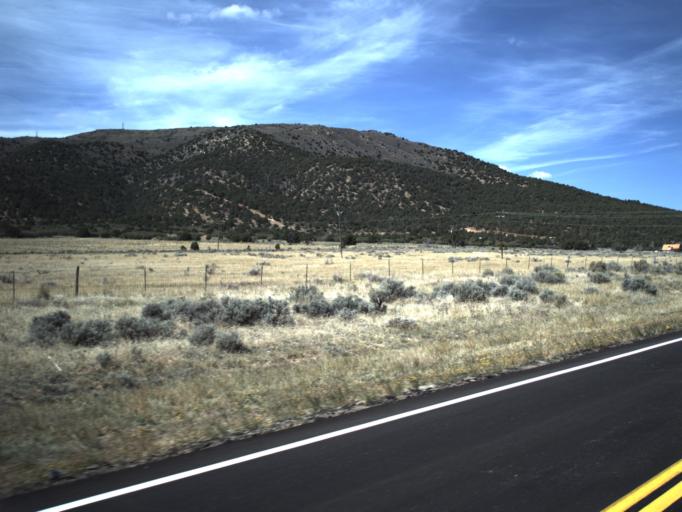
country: US
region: Utah
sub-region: Washington County
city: Enterprise
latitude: 37.4983
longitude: -113.6313
